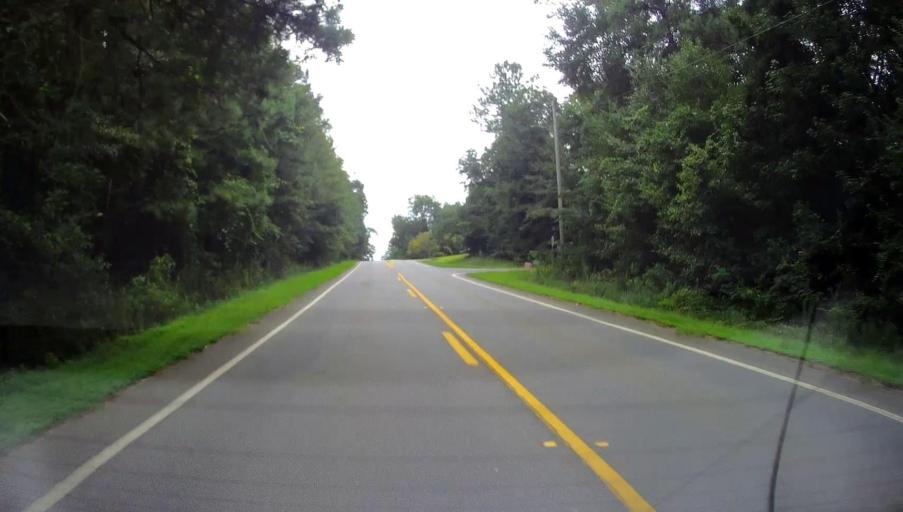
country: US
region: Georgia
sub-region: Schley County
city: Ellaville
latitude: 32.2418
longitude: -84.3176
